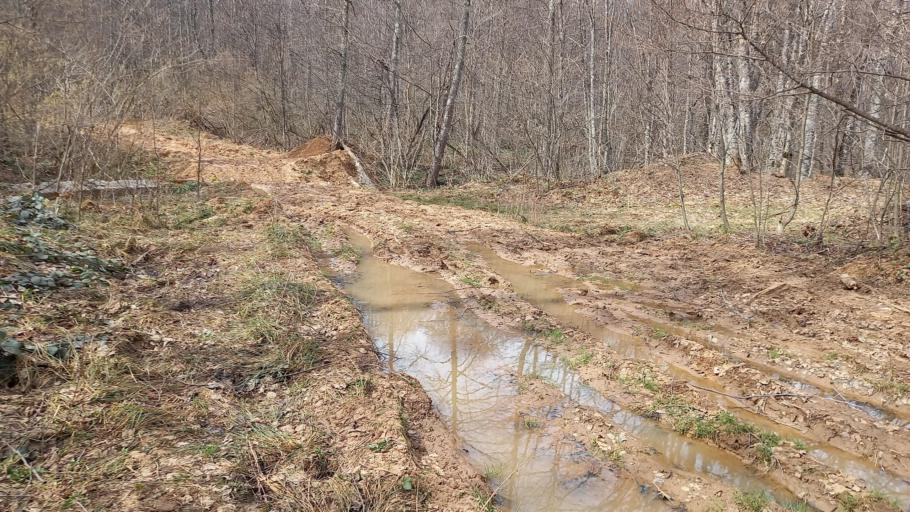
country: RU
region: Adygeya
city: Kamennomostskiy
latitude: 44.2193
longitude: 40.0839
